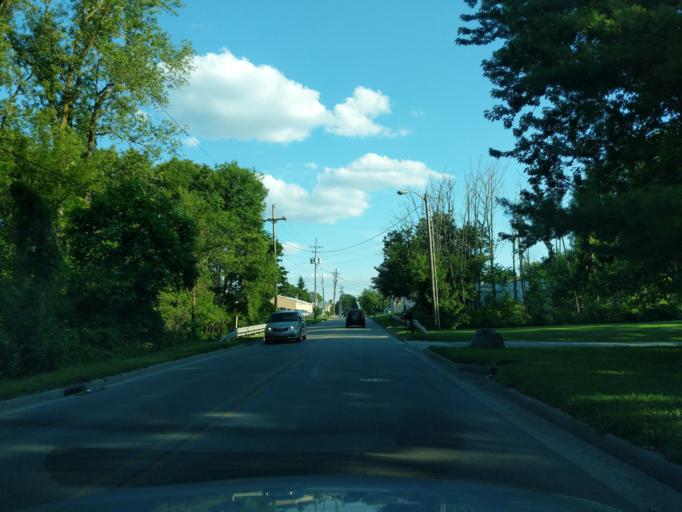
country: US
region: Indiana
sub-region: Huntington County
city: Huntington
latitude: 40.8851
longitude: -85.4712
